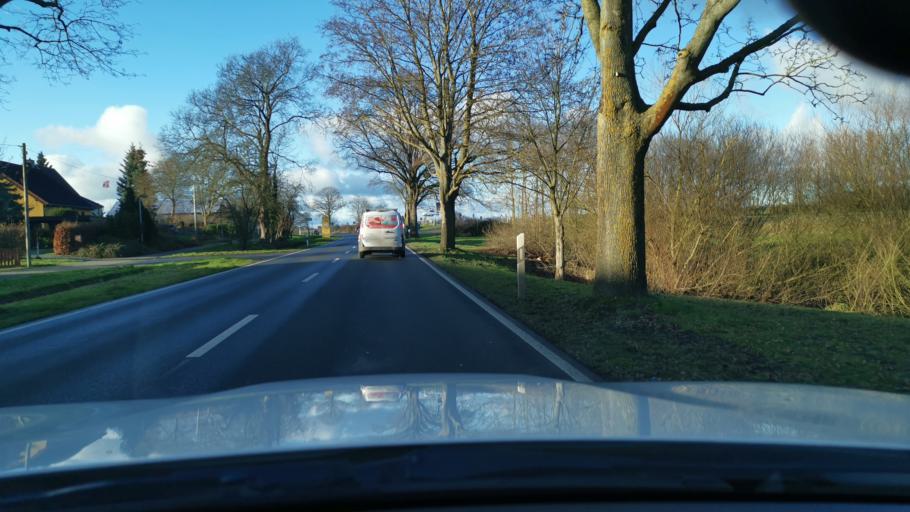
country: DE
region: Mecklenburg-Vorpommern
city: Tessin
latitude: 54.0333
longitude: 12.4448
